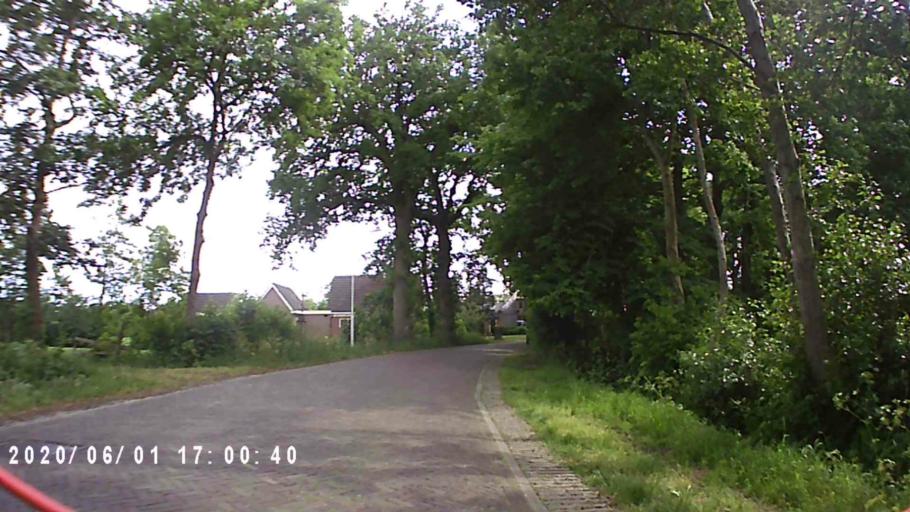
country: NL
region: Friesland
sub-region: Gemeente Tytsjerksteradiel
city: Hurdegaryp
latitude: 53.1824
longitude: 5.9297
